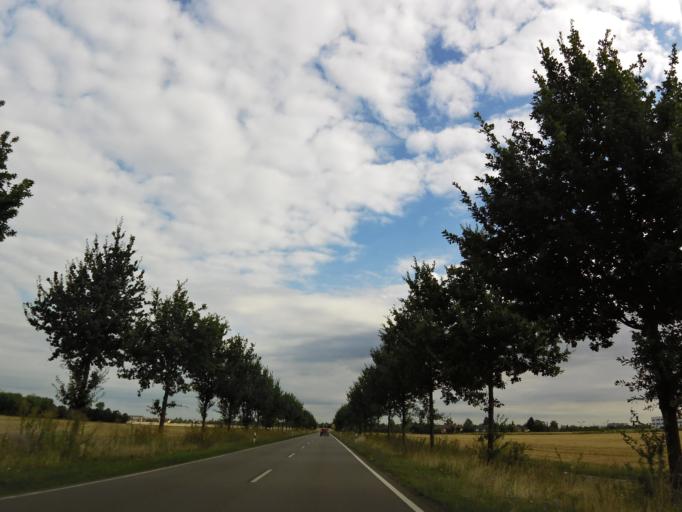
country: DE
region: Saxony
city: Markkleeberg
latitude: 51.2974
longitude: 12.3033
